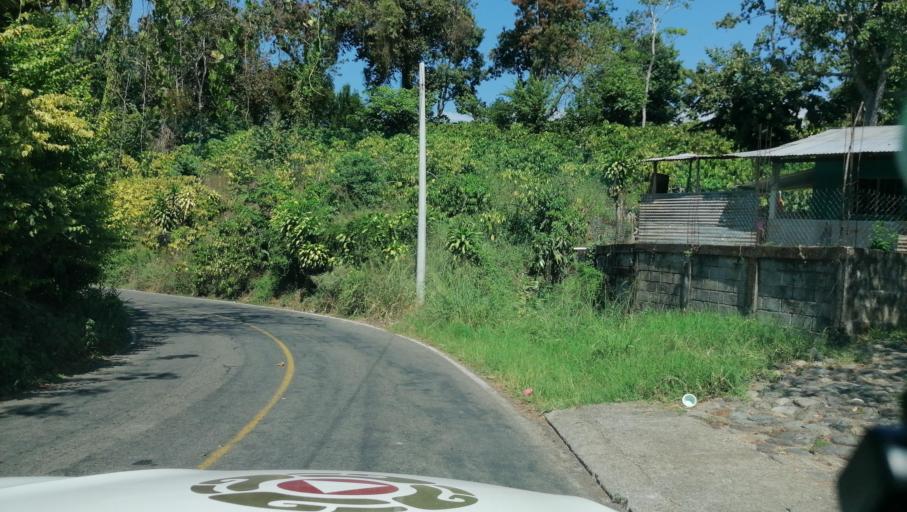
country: MX
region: Chiapas
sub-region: Cacahoatan
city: Benito Juarez
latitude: 15.0226
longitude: -92.2200
